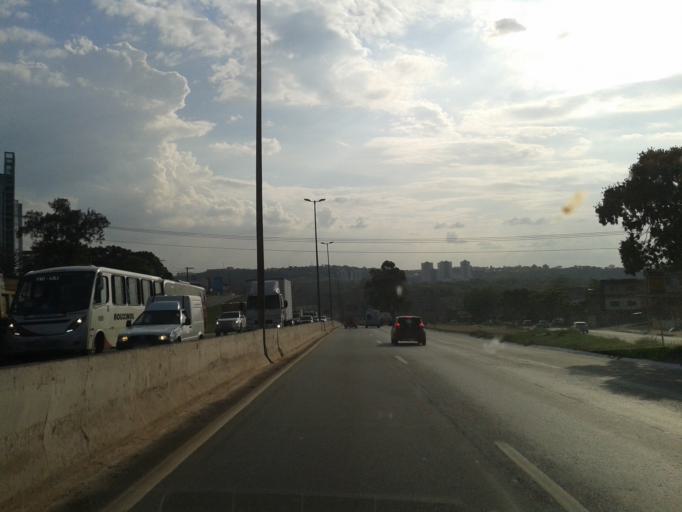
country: BR
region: Minas Gerais
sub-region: Belo Horizonte
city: Belo Horizonte
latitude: -19.8825
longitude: -43.9602
